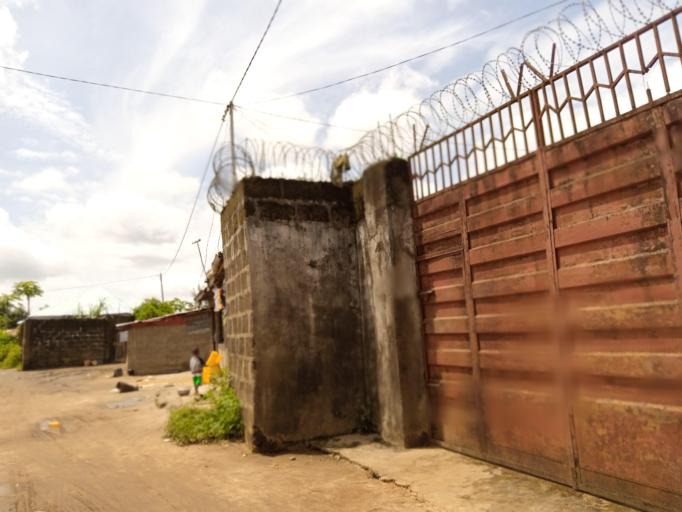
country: SL
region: Northern Province
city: Masoyila
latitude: 8.6038
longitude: -13.1823
